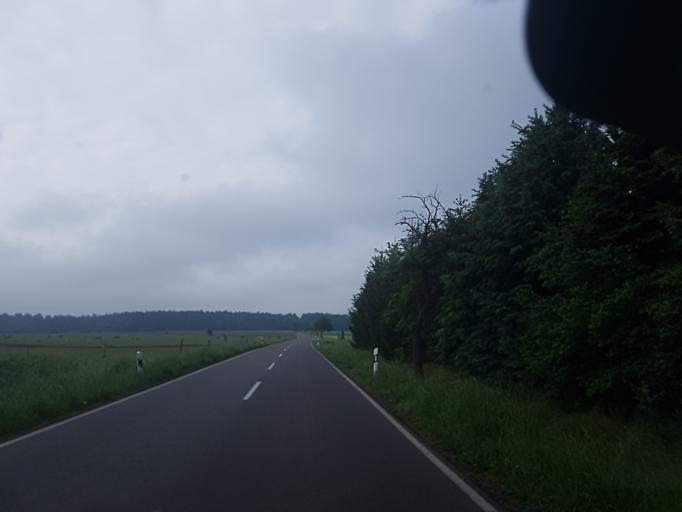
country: DE
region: Saxony-Anhalt
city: Klieken
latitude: 52.0072
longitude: 12.3730
